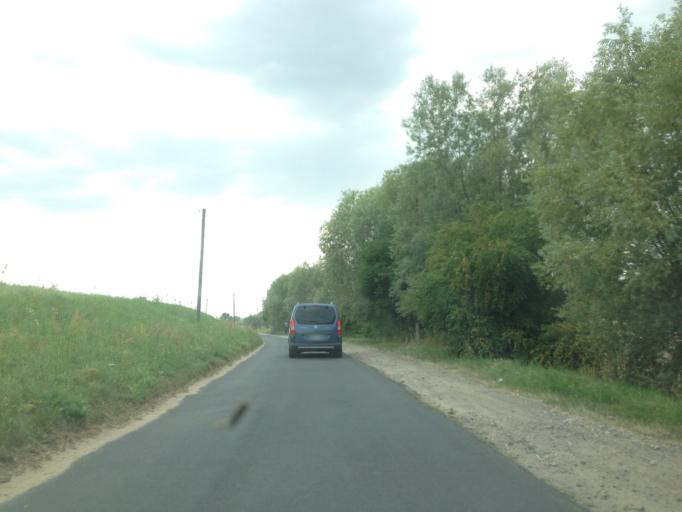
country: PL
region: Kujawsko-Pomorskie
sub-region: Powiat chelminski
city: Chelmno
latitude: 53.3758
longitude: 18.4156
